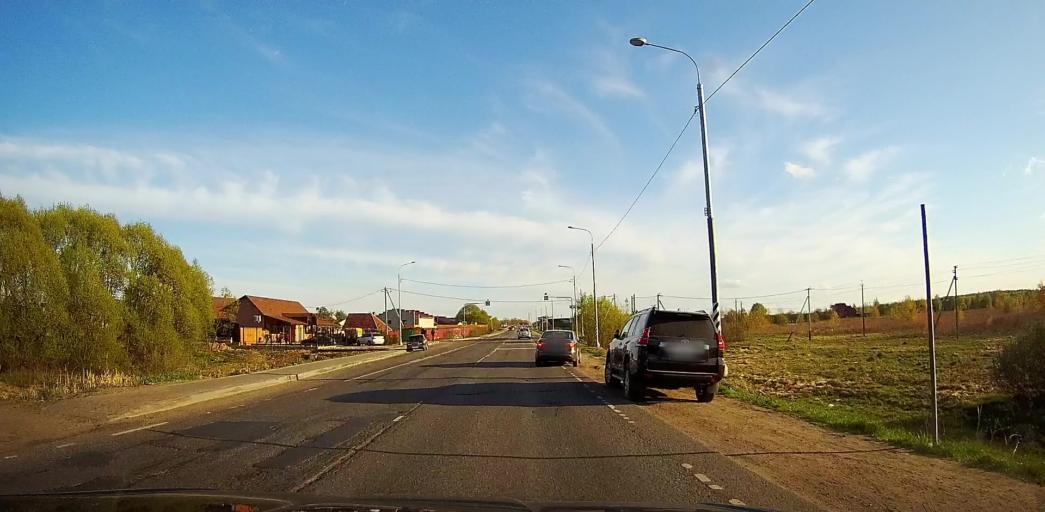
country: RU
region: Moskovskaya
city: Bronnitsy
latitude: 55.3294
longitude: 38.2195
